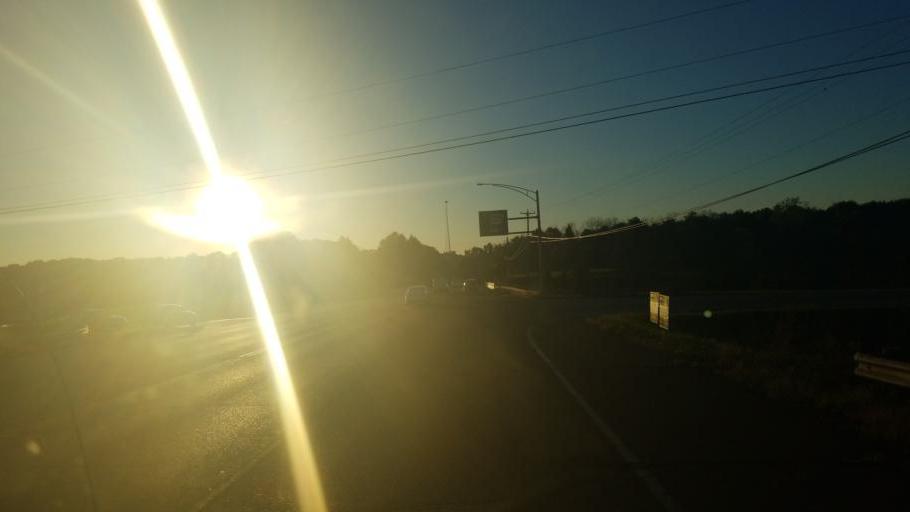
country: US
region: Ohio
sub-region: Stark County
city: Alliance
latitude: 40.9022
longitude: -81.1679
